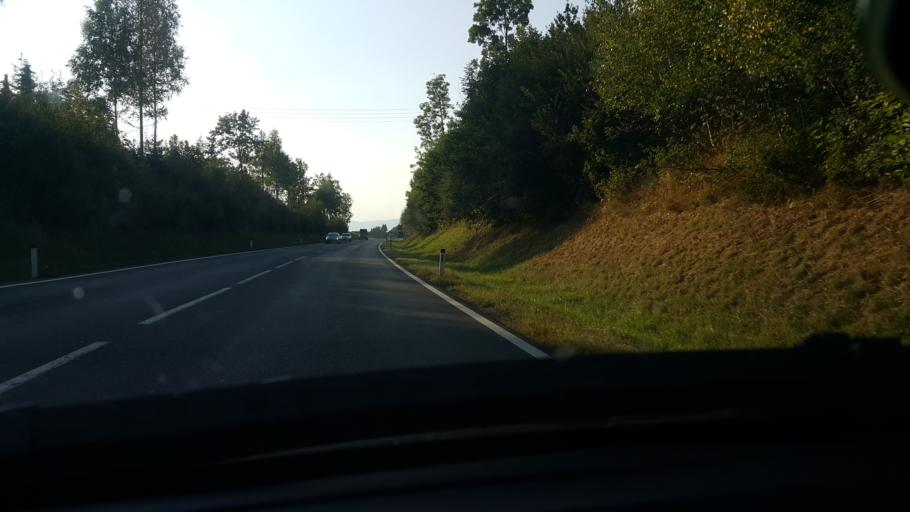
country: AT
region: Carinthia
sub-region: Politischer Bezirk Klagenfurt Land
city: Moosburg
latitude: 46.6861
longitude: 14.1437
